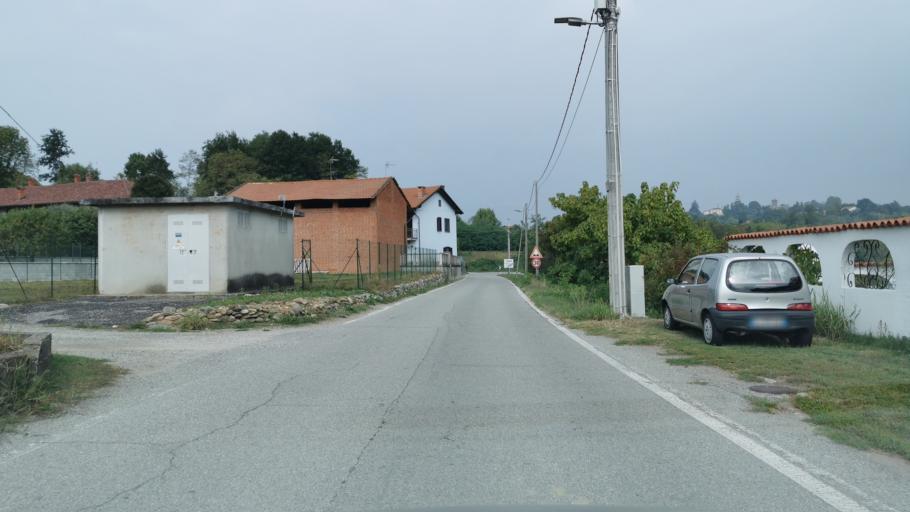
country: IT
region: Piedmont
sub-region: Provincia di Torino
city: Tonengo-Casale
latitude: 45.2939
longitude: 7.9426
